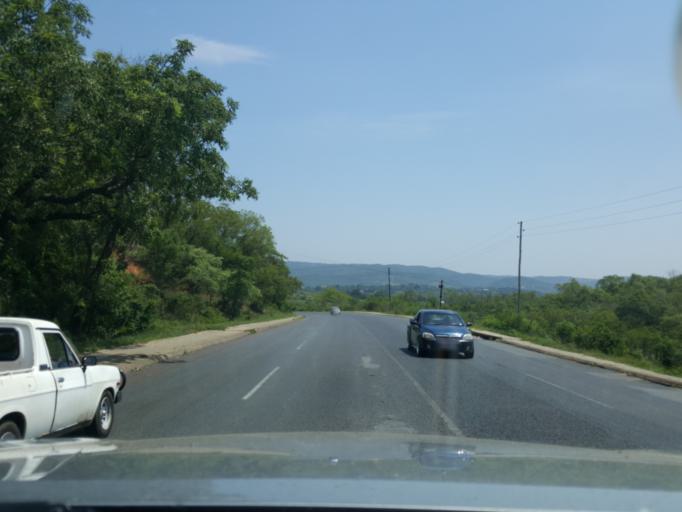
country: ZA
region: Mpumalanga
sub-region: Ehlanzeni District
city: White River
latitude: -25.0597
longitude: 31.1302
